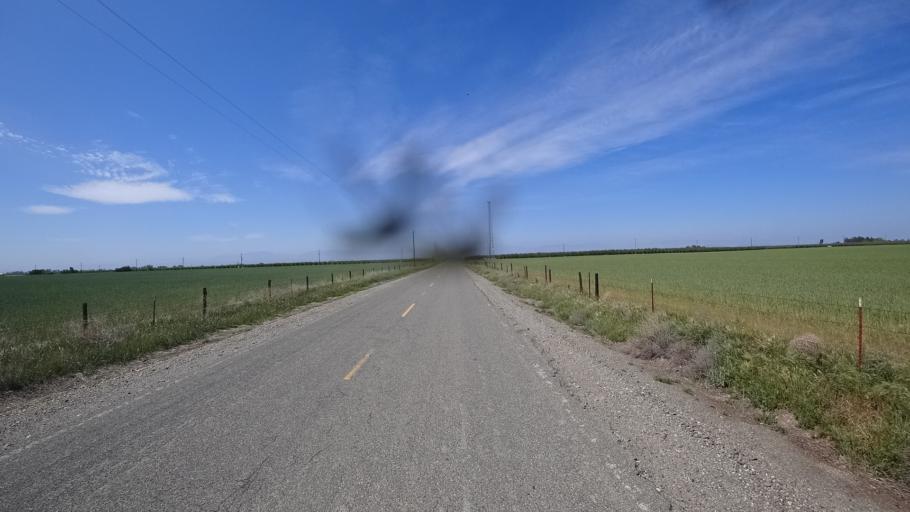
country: US
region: California
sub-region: Glenn County
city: Orland
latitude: 39.6531
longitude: -122.1745
